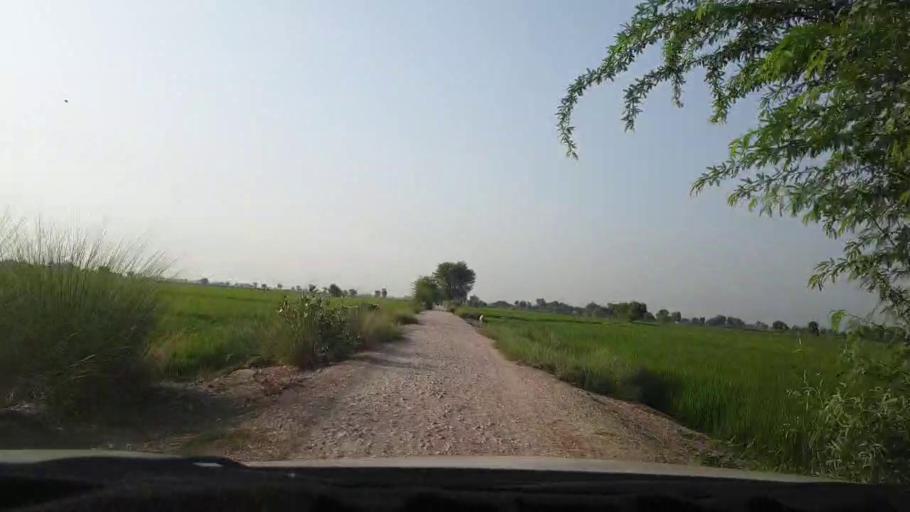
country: PK
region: Sindh
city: Larkana
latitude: 27.5082
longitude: 68.1730
